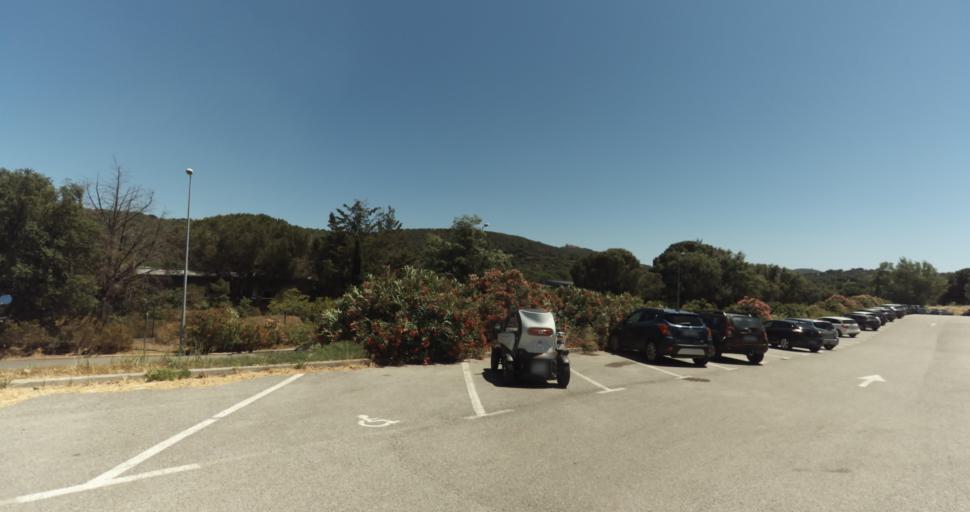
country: FR
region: Provence-Alpes-Cote d'Azur
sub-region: Departement du Var
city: Gassin
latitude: 43.2491
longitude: 6.5724
